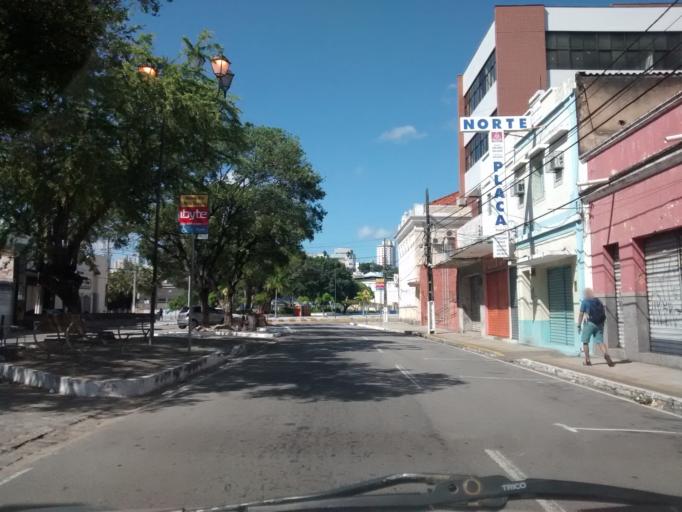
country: BR
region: Rio Grande do Norte
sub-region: Natal
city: Natal
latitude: -5.7787
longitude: -35.2050
